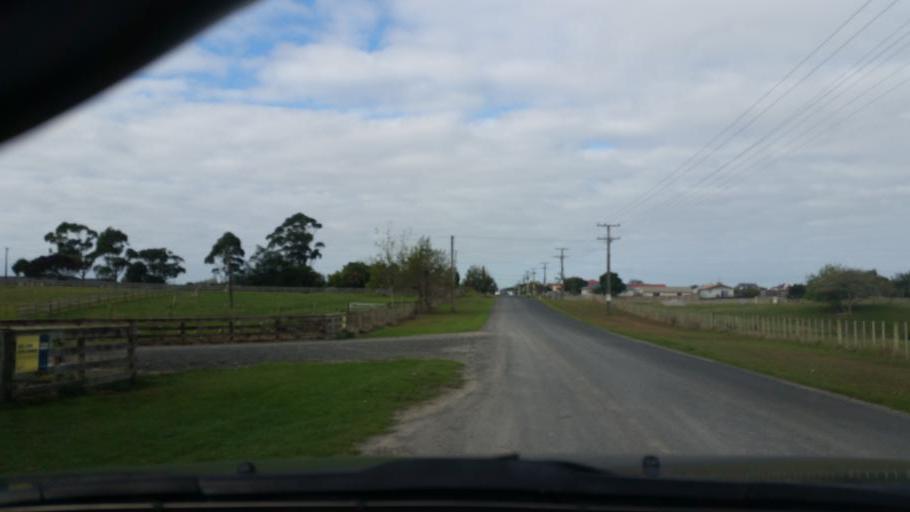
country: NZ
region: Northland
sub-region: Kaipara District
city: Dargaville
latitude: -35.9222
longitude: 173.8678
